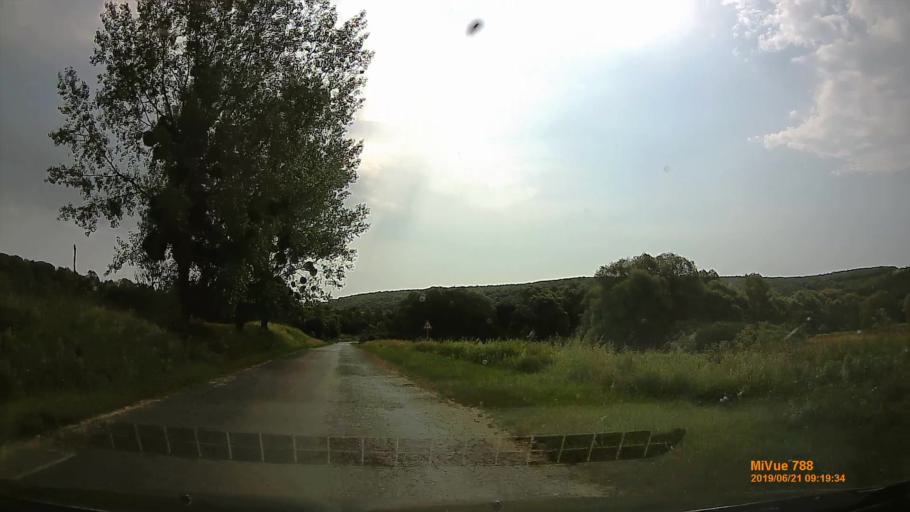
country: HU
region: Somogy
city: Taszar
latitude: 46.2327
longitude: 17.8643
